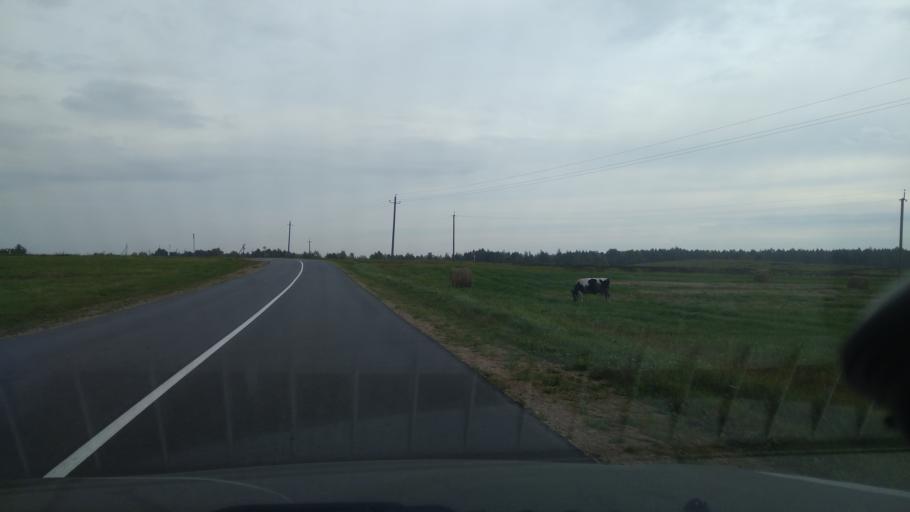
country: BY
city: Michanovichi
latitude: 53.6146
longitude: 27.7149
